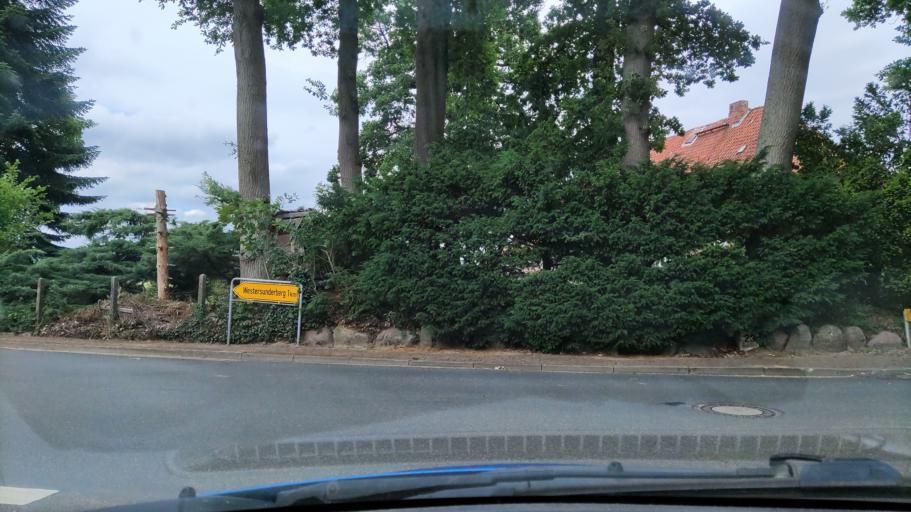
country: DE
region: Lower Saxony
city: Weste
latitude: 53.0607
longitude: 10.7031
